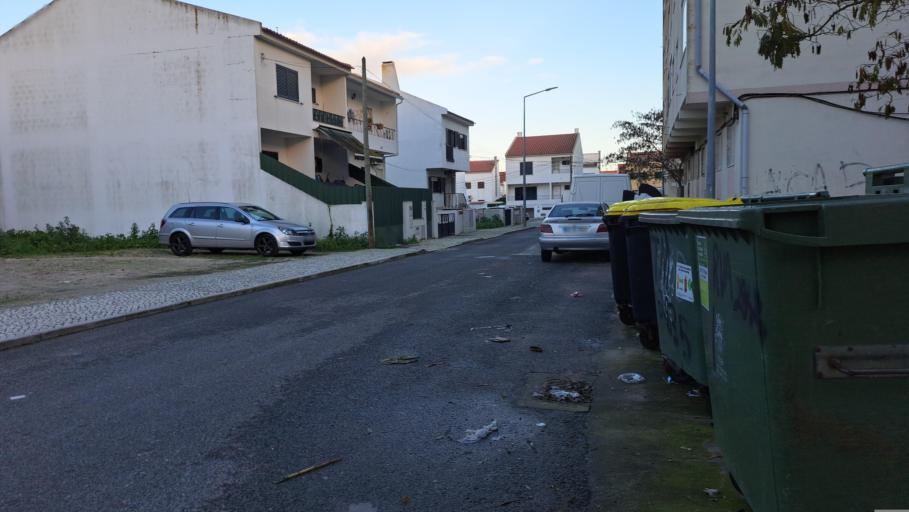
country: PT
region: Setubal
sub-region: Moita
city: Alhos Vedros
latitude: 38.6458
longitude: -9.0376
